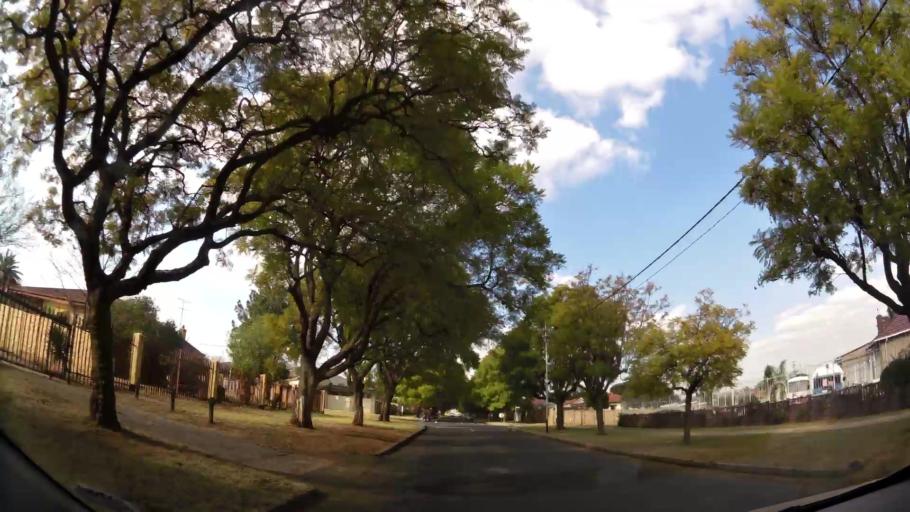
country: ZA
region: Gauteng
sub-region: West Rand District Municipality
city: Krugersdorp
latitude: -26.0901
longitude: 27.7655
